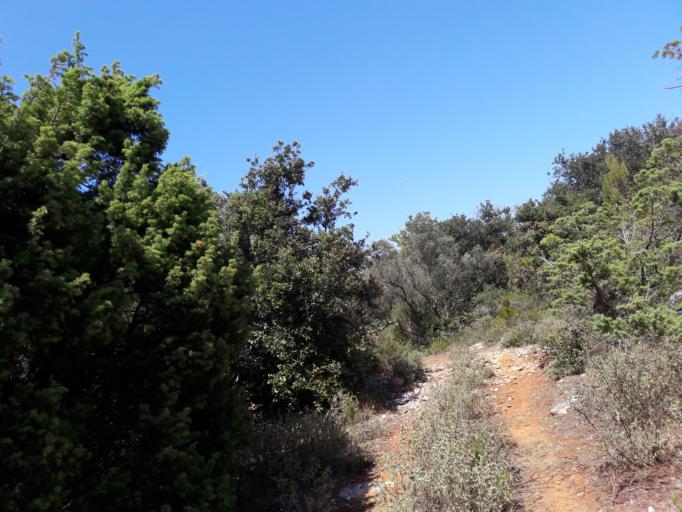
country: HR
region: Licko-Senjska
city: Novalja
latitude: 44.3645
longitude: 14.6983
